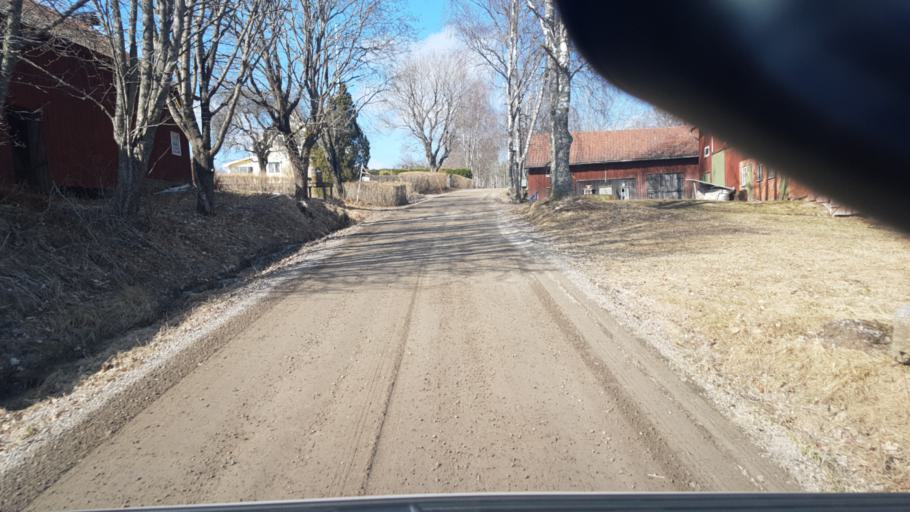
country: SE
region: Vaermland
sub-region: Eda Kommun
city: Amotfors
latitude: 59.8321
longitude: 12.3579
